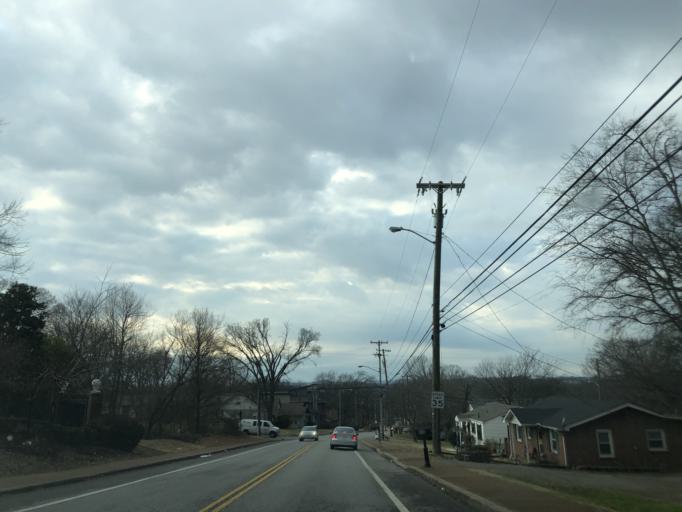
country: US
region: Tennessee
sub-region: Davidson County
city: Nashville
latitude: 36.1953
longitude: -86.7299
